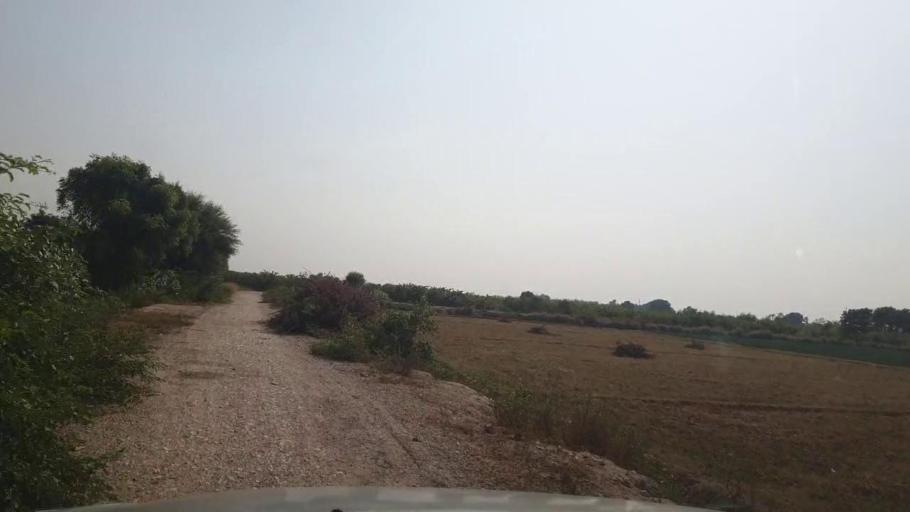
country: PK
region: Sindh
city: Bhit Shah
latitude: 25.7308
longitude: 68.4969
